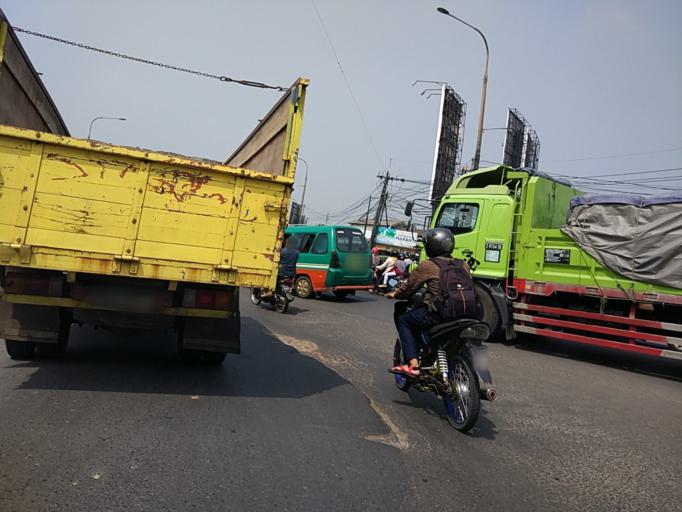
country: ID
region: West Java
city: Padalarang
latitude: -6.8513
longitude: 107.4972
